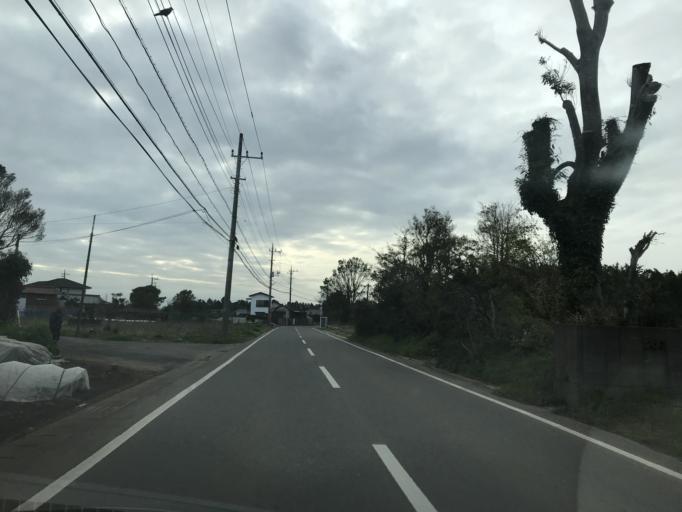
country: JP
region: Chiba
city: Omigawa
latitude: 35.7988
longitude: 140.5828
